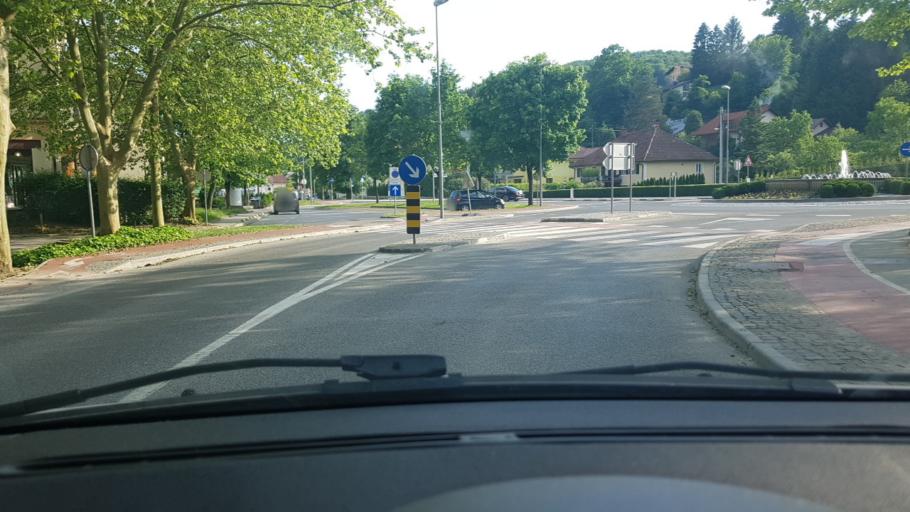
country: SI
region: Rogaska Slatina
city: Rogaska Slatina
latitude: 46.2345
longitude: 15.6382
